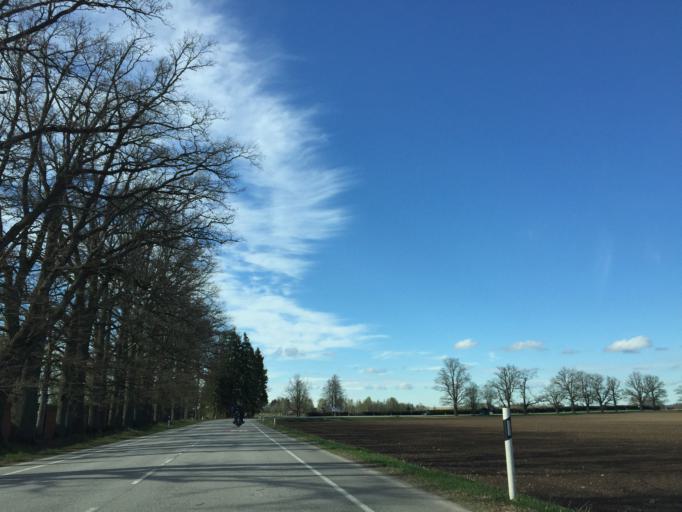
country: EE
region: Vorumaa
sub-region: Antsla vald
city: Vana-Antsla
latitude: 57.9023
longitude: 26.2865
